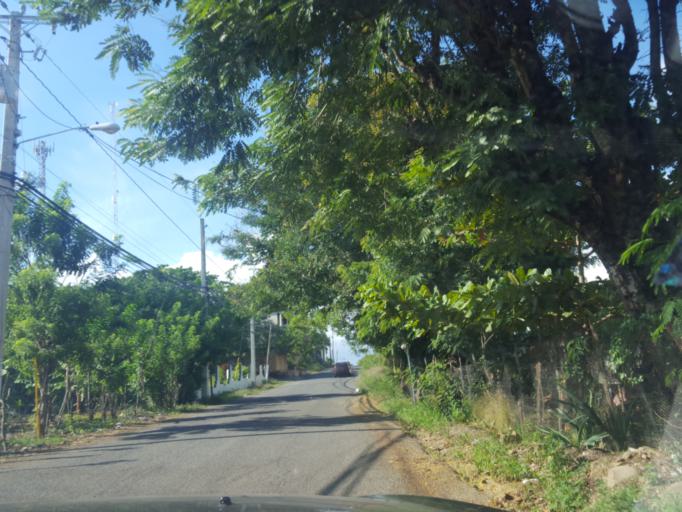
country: DO
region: La Vega
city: Rio Verde Arriba
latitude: 19.3476
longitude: -70.6036
